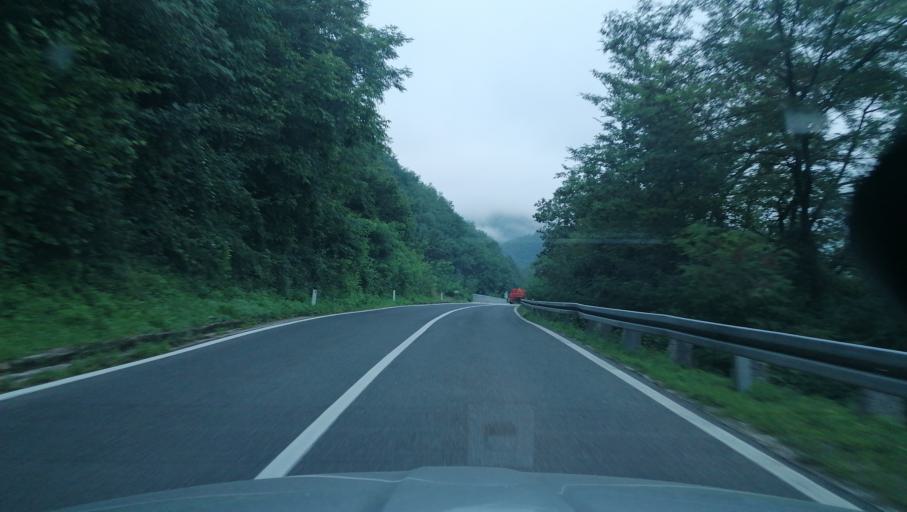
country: BA
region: Federation of Bosnia and Herzegovina
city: Jablanica
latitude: 43.7173
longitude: 17.7113
